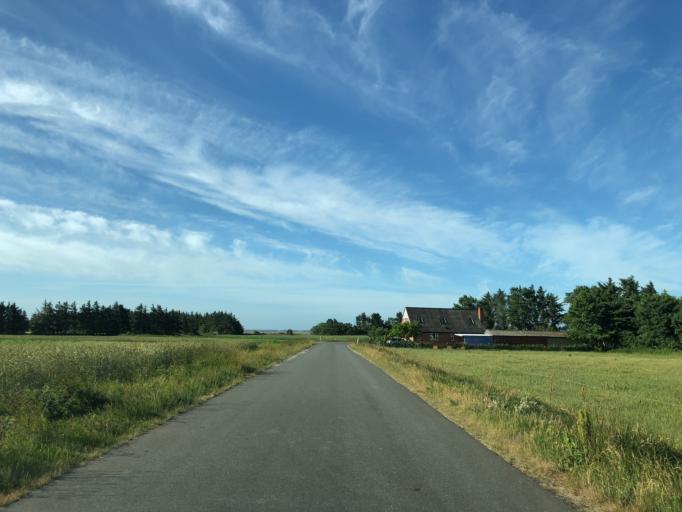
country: DK
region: Central Jutland
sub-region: Holstebro Kommune
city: Ulfborg
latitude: 56.3357
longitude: 8.2711
